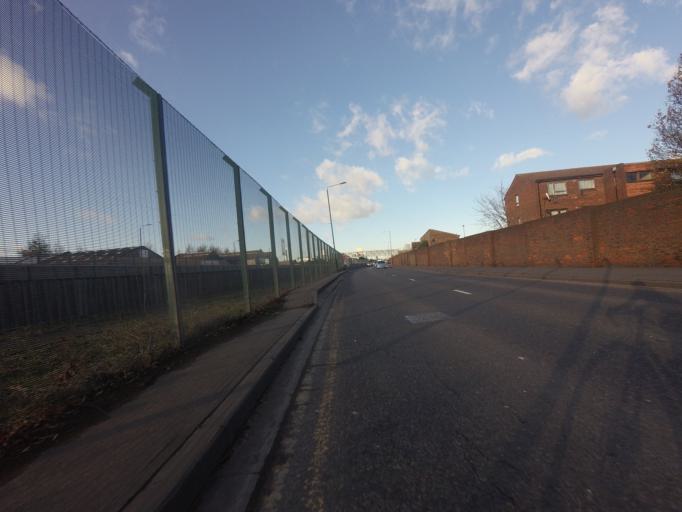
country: GB
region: England
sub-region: Greater London
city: Poplar
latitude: 51.5191
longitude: 0.0048
